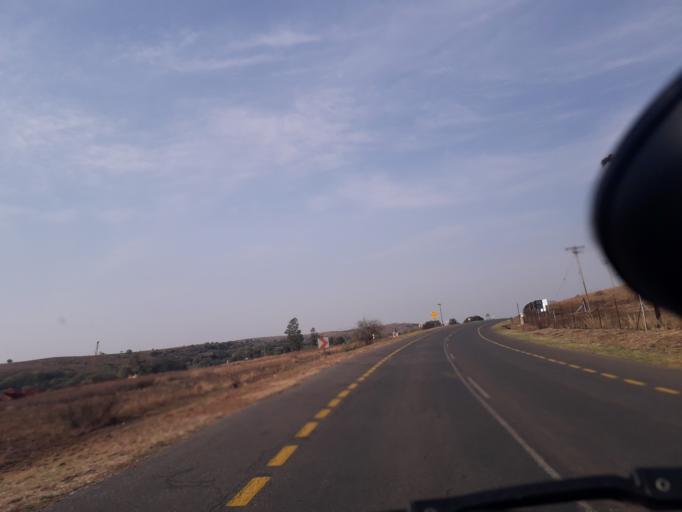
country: ZA
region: Gauteng
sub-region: West Rand District Municipality
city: Krugersdorp
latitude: -26.0151
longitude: 27.7314
